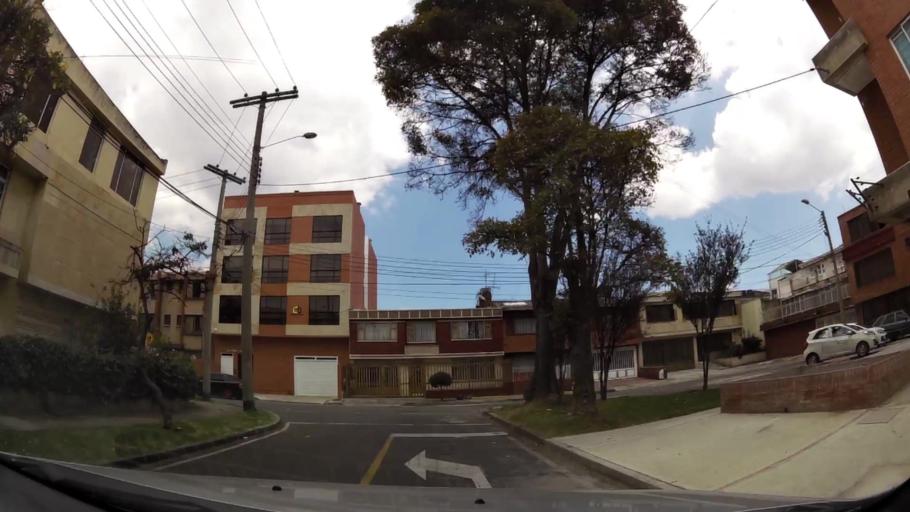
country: CO
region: Bogota D.C.
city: Bogota
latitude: 4.5860
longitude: -74.0920
